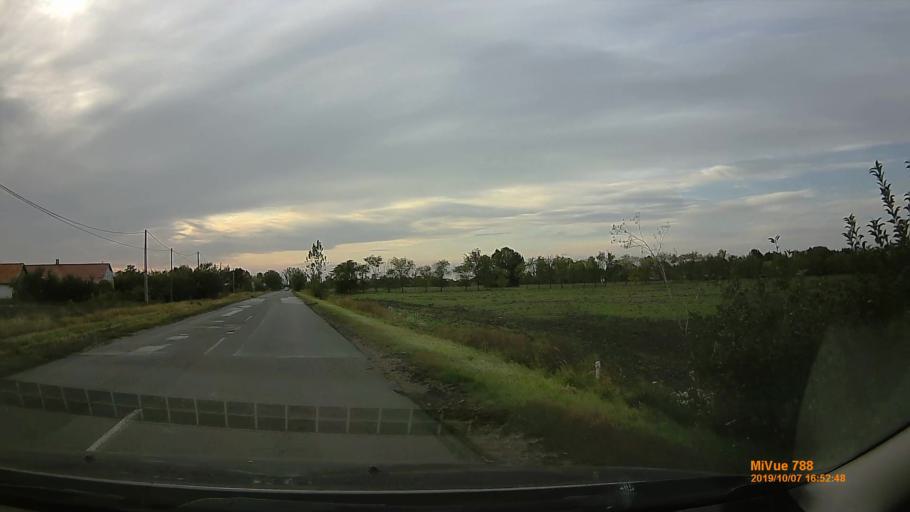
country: HU
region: Bekes
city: Szarvas
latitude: 46.8282
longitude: 20.5873
